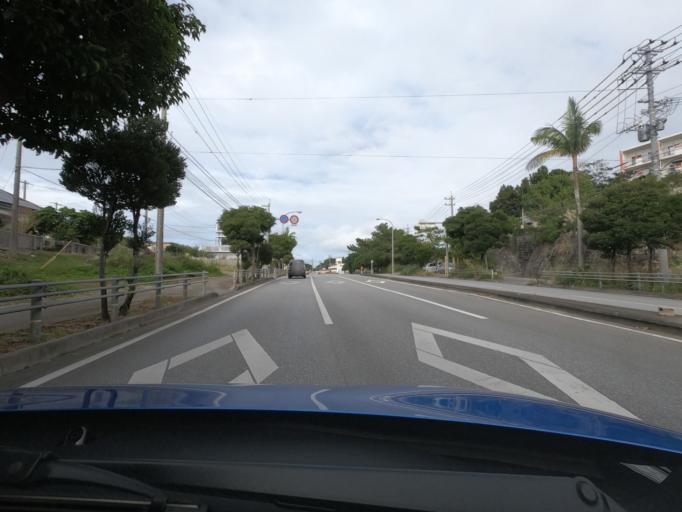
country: JP
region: Okinawa
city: Nago
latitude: 26.6729
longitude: 127.8901
